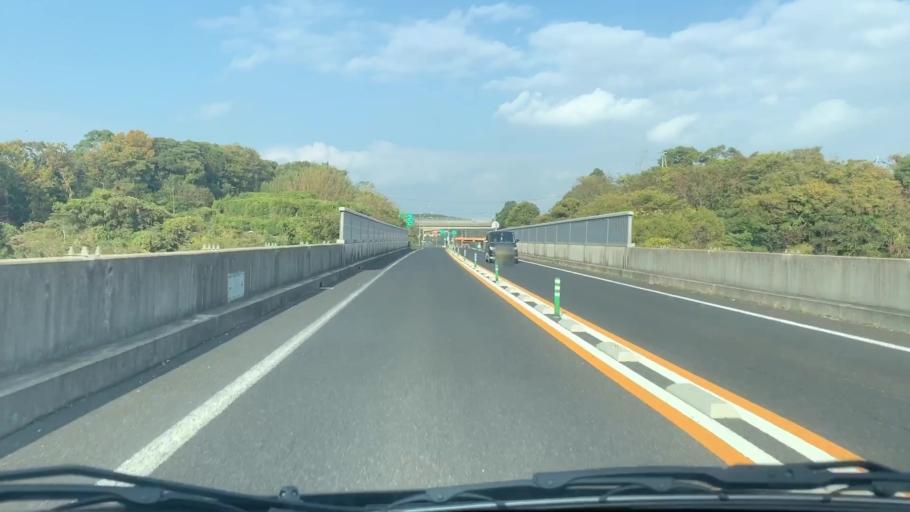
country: JP
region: Nagasaki
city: Sasebo
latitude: 33.0619
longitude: 129.7597
